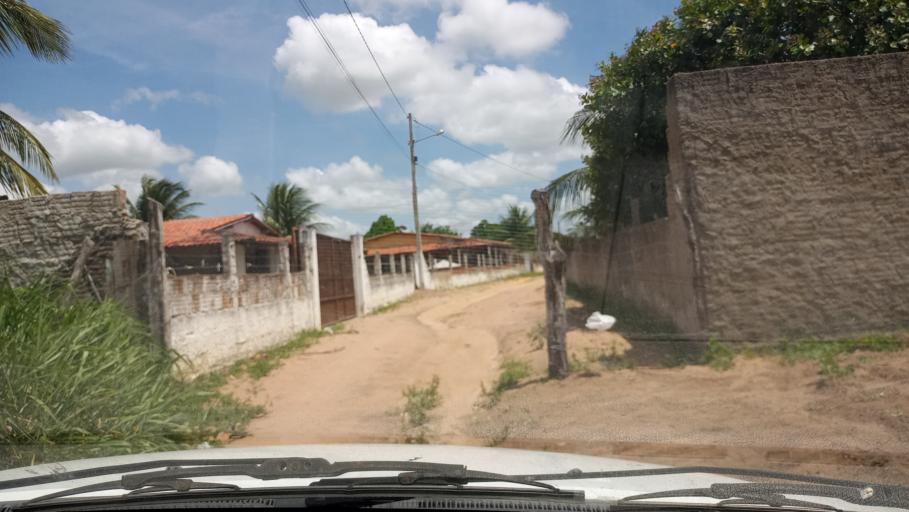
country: BR
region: Rio Grande do Norte
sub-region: Brejinho
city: Brejinho
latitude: -6.2642
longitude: -35.3704
